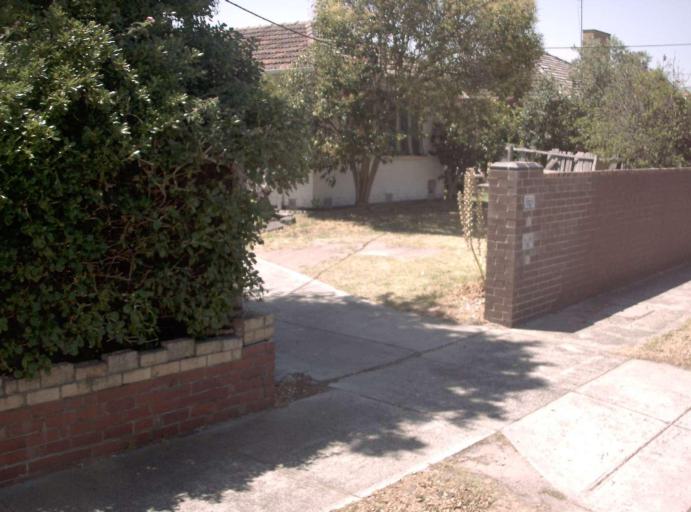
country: AU
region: Victoria
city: Hughesdale
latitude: -37.9101
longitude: 145.0908
